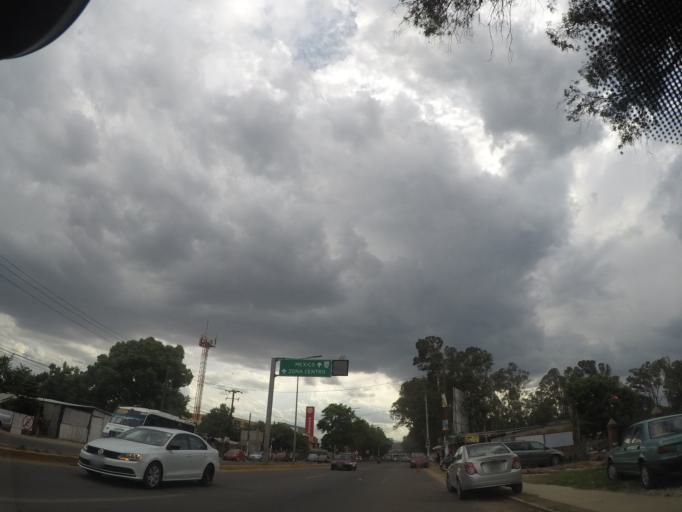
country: MX
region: Oaxaca
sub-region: Santa Cruz Amilpas
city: Santa Cruz Amilpas
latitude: 17.0688
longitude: -96.6928
